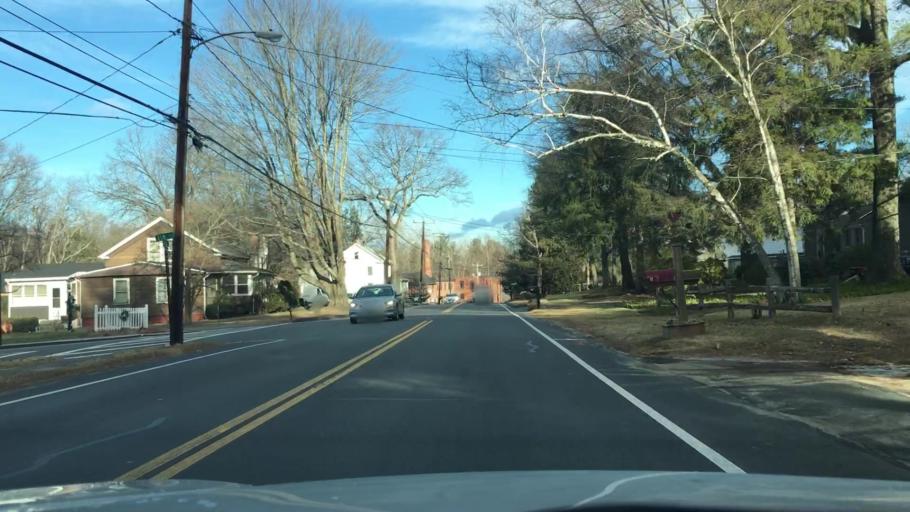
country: US
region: Massachusetts
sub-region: Hampden County
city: Agawam
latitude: 42.0646
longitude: -72.6253
